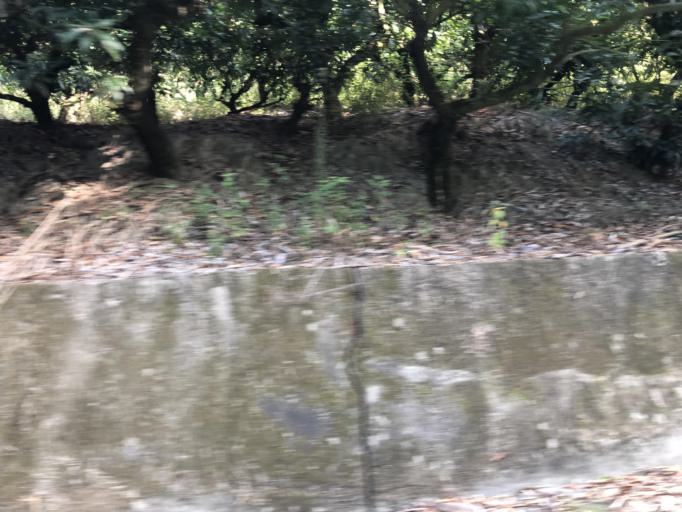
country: TW
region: Taiwan
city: Yujing
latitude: 23.0237
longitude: 120.3951
